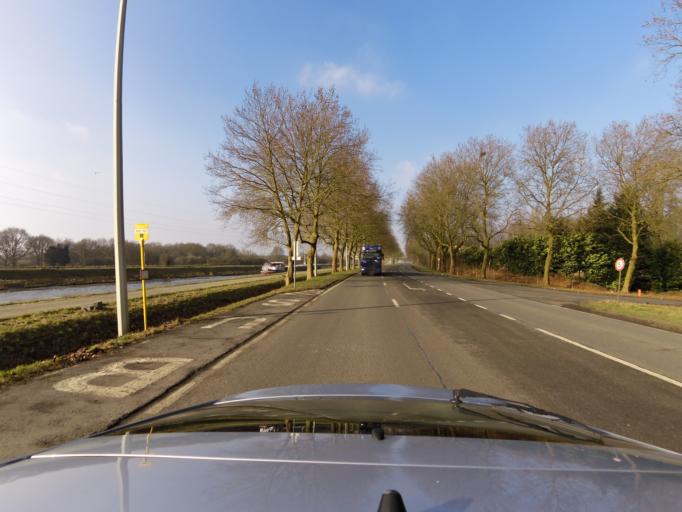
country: BE
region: Wallonia
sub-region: Province du Hainaut
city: Saint-Ghislain
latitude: 50.4742
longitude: 3.8071
